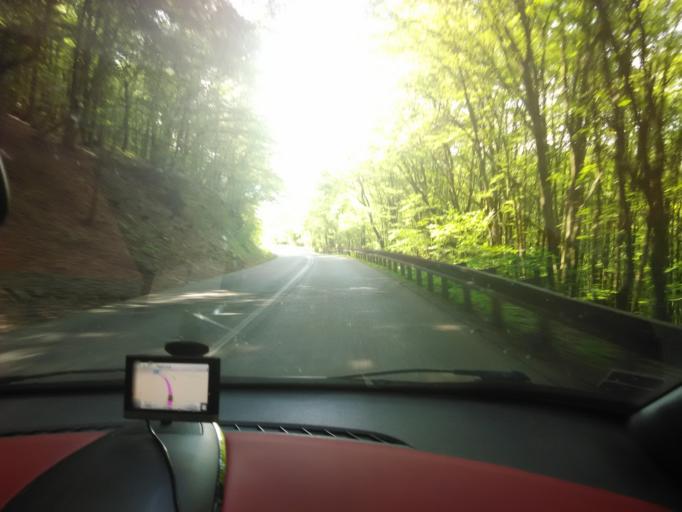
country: SK
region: Banskobystricky
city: Revuca
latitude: 48.6284
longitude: 20.2656
